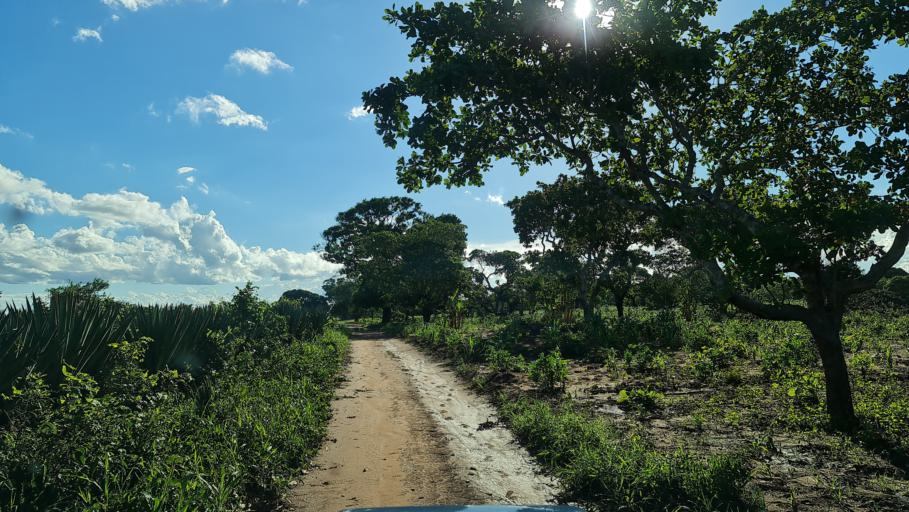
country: MZ
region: Nampula
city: Ilha de Mocambique
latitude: -14.9361
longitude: 40.2051
